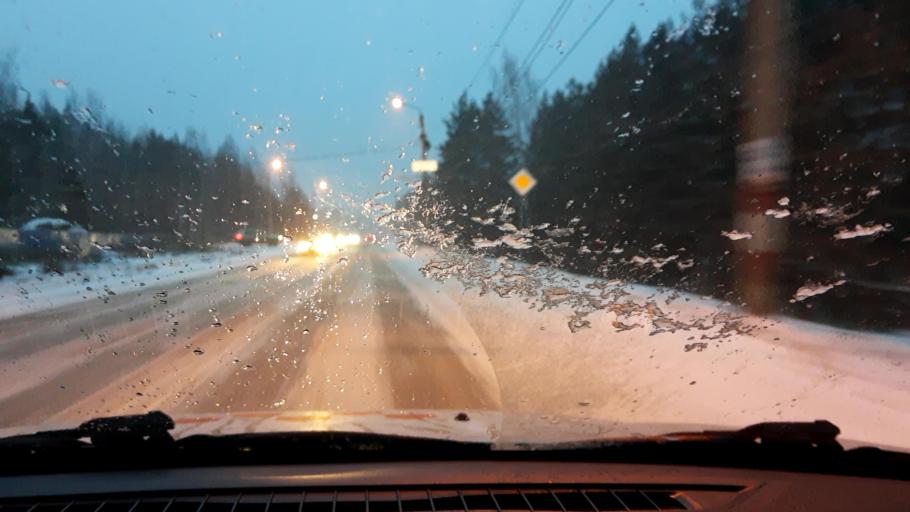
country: RU
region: Nizjnij Novgorod
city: Bor
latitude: 56.3257
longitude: 44.1369
